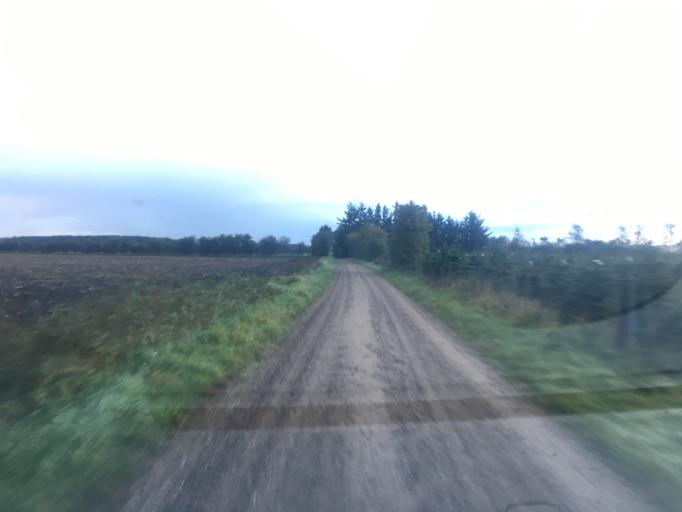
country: DK
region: South Denmark
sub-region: Tonder Kommune
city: Logumkloster
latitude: 54.9919
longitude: 9.0265
